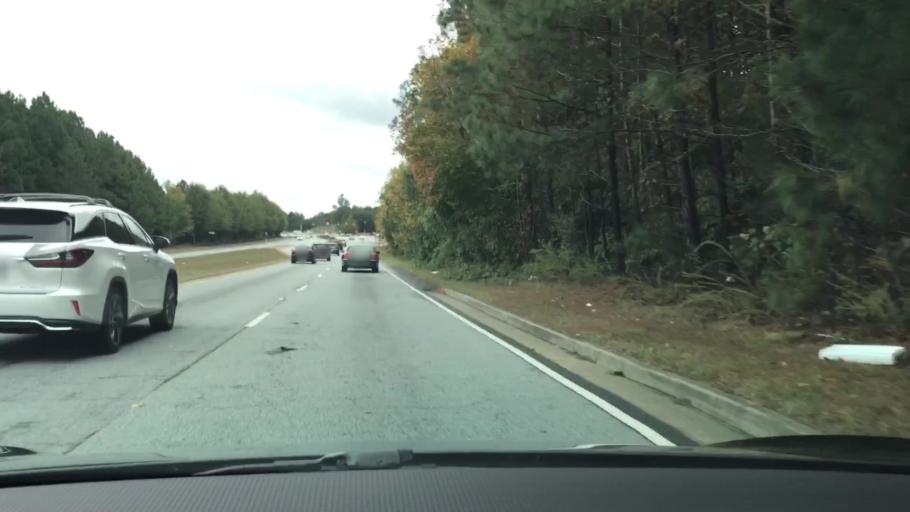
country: US
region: Georgia
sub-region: Gwinnett County
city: Suwanee
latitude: 34.0340
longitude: -84.0700
